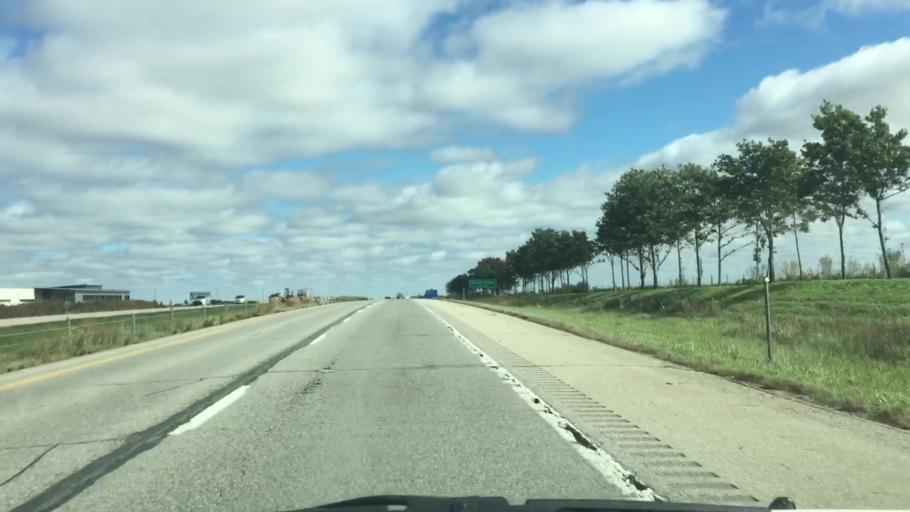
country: US
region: Iowa
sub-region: Poweshiek County
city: Grinnell
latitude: 41.6952
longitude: -92.7434
